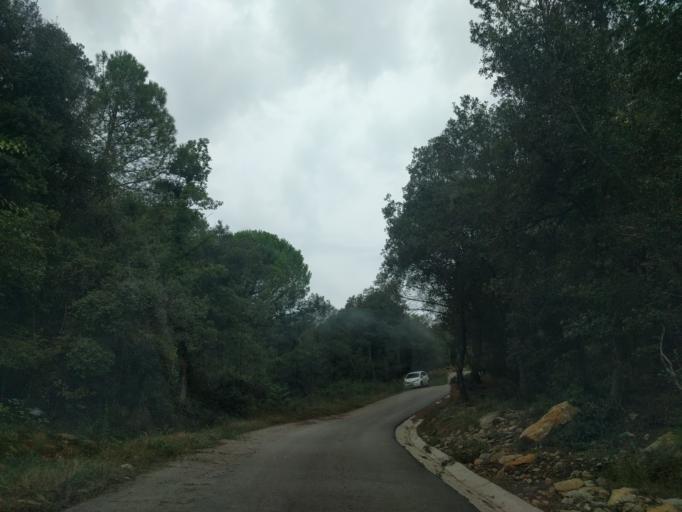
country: ES
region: Catalonia
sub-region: Provincia de Girona
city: la Cellera de Ter
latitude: 42.0194
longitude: 2.6303
